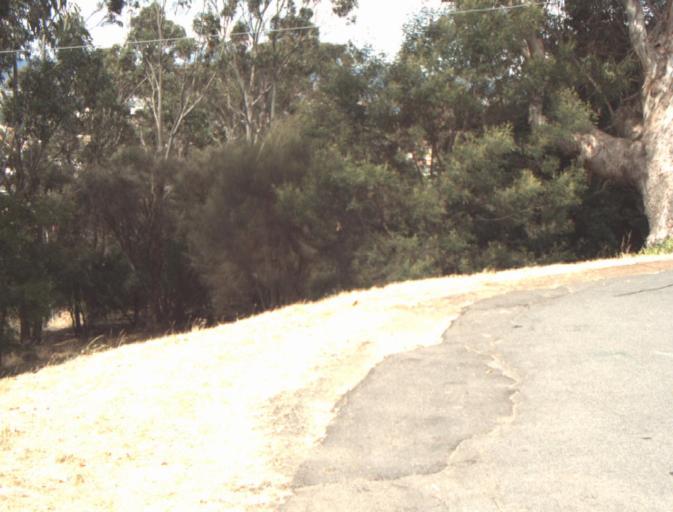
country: AU
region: Tasmania
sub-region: Launceston
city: Launceston
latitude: -41.4427
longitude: 147.1269
